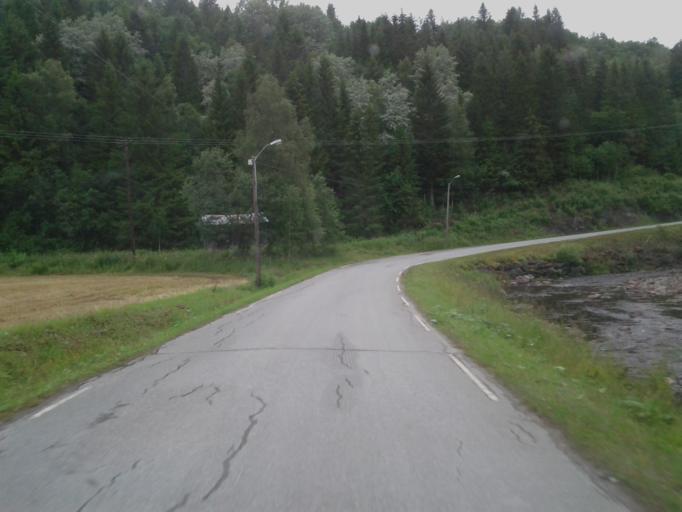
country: NO
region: Sor-Trondelag
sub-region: Melhus
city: Lundamo
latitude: 63.1389
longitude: 10.3263
